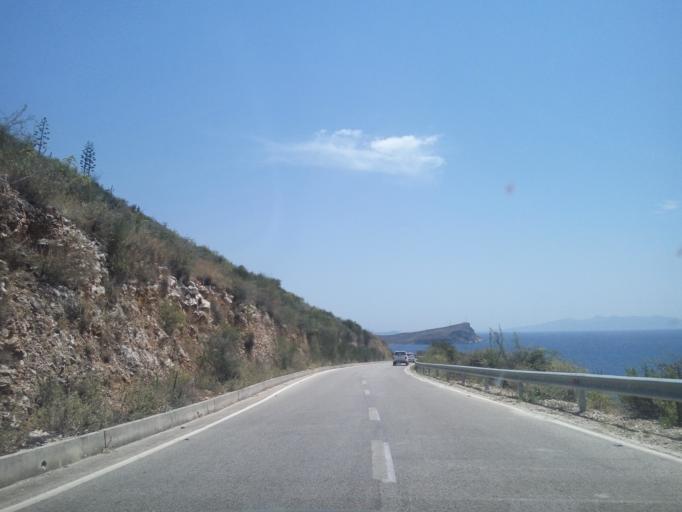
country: AL
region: Vlore
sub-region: Rrethi i Vlores
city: Himare
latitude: 40.0753
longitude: 19.7790
